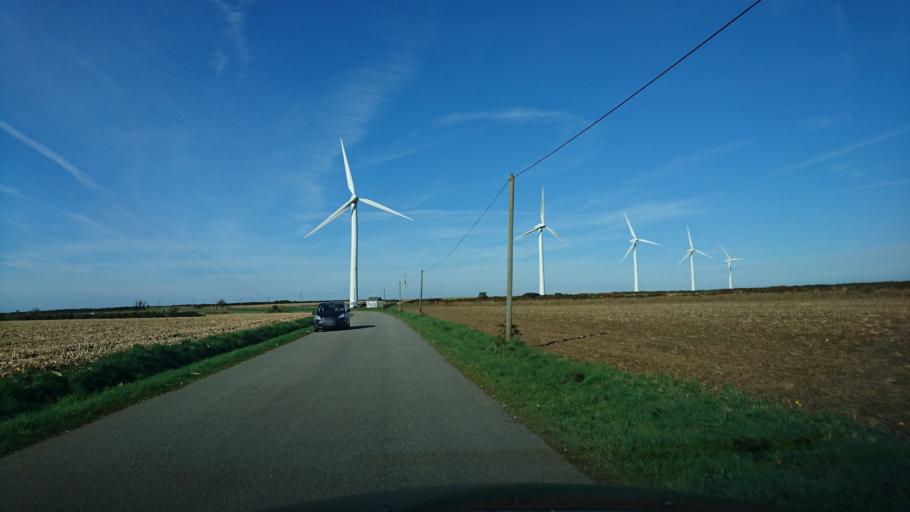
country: FR
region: Brittany
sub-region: Departement du Finistere
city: Plouarzel
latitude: 48.4271
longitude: -4.7452
